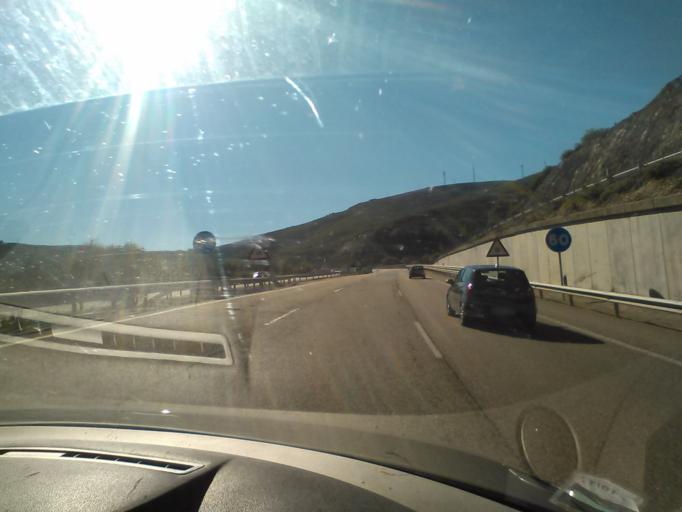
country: ES
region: Castille and Leon
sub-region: Provincia de Zamora
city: Lubian
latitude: 42.0388
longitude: -6.9484
